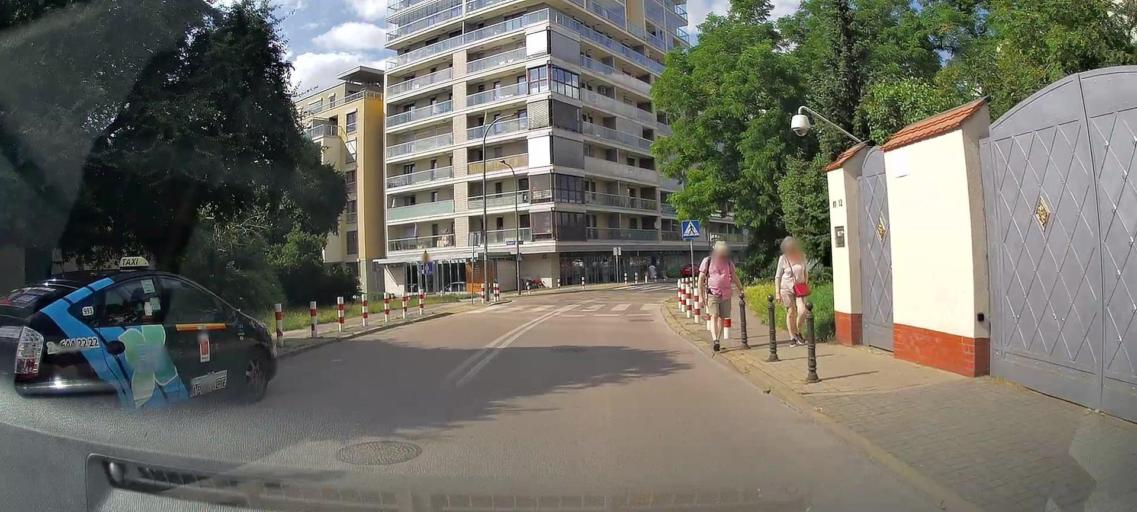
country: PL
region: Masovian Voivodeship
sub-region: Warszawa
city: Mokotow
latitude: 52.1667
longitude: 21.0119
